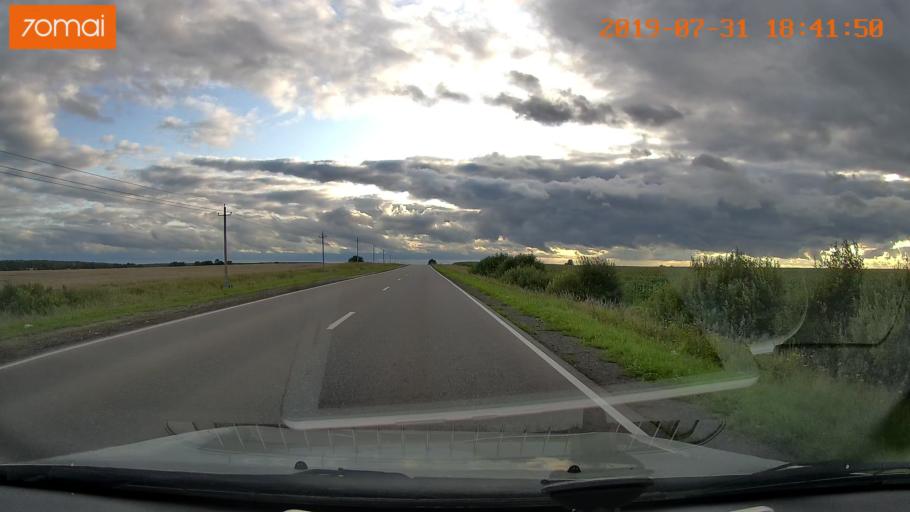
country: RU
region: Moskovskaya
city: Voskresensk
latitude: 55.2526
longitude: 38.6032
